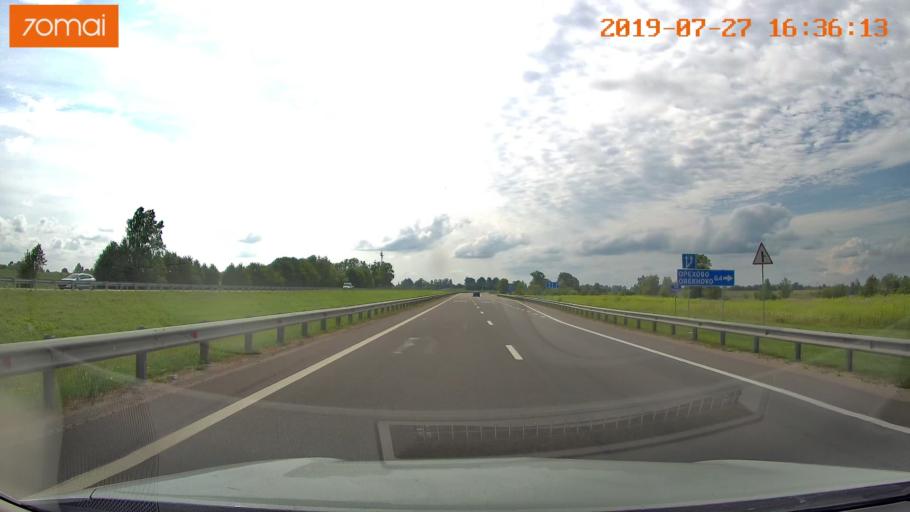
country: RU
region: Kaliningrad
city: Gvardeysk
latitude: 54.6486
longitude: 21.2894
